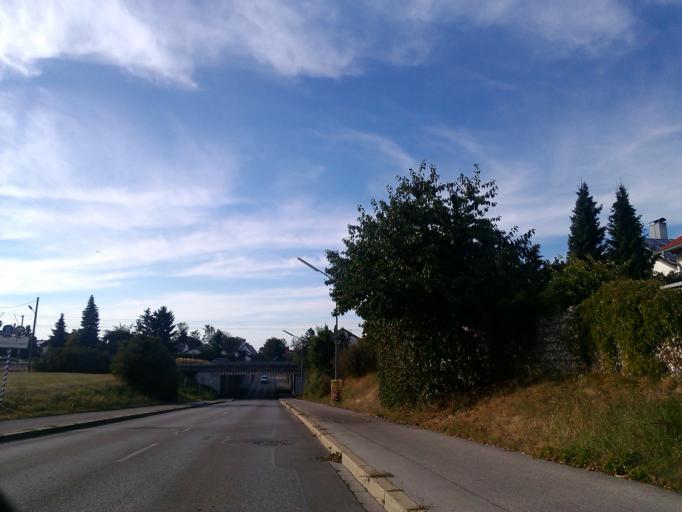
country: DE
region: Bavaria
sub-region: Upper Bavaria
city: Germering
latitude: 48.1257
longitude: 11.3556
